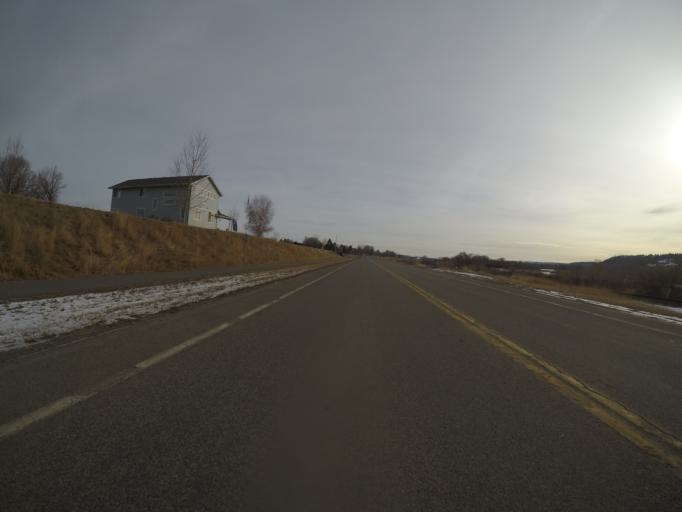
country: US
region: Montana
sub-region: Stillwater County
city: Columbus
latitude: 45.6408
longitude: -109.2699
